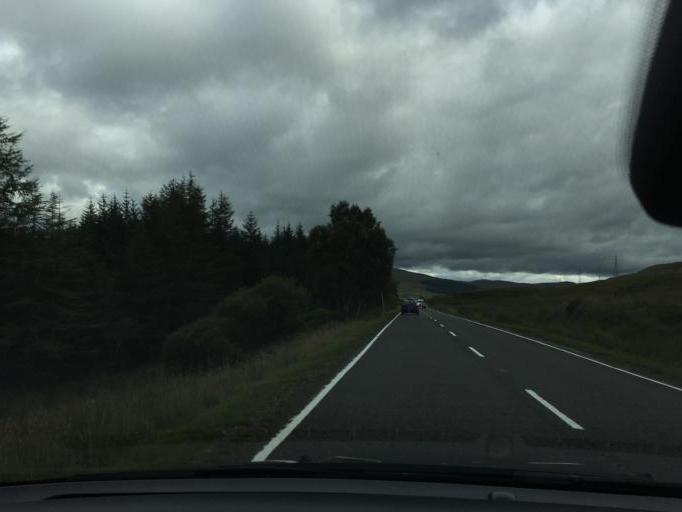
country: GB
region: Scotland
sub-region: Highland
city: Spean Bridge
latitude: 56.5453
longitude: -4.7599
